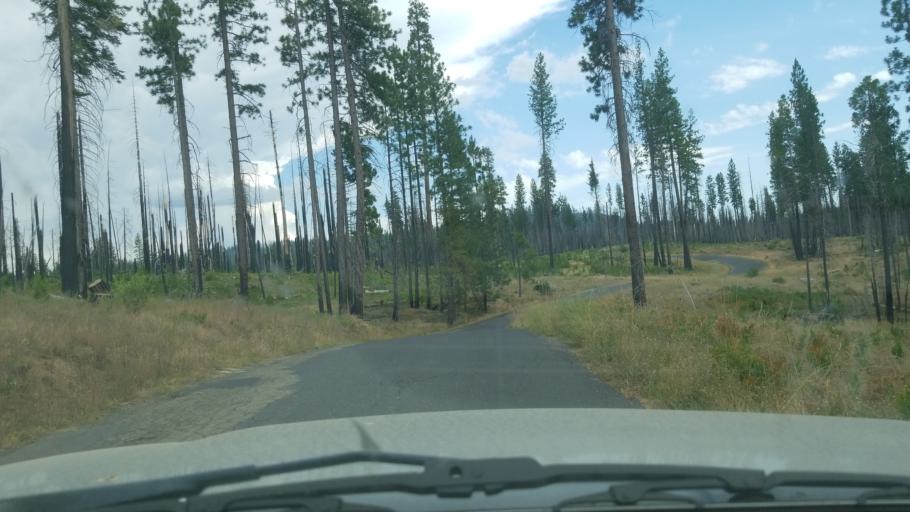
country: US
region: California
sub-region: Mariposa County
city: Yosemite Valley
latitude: 37.8437
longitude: -119.8539
